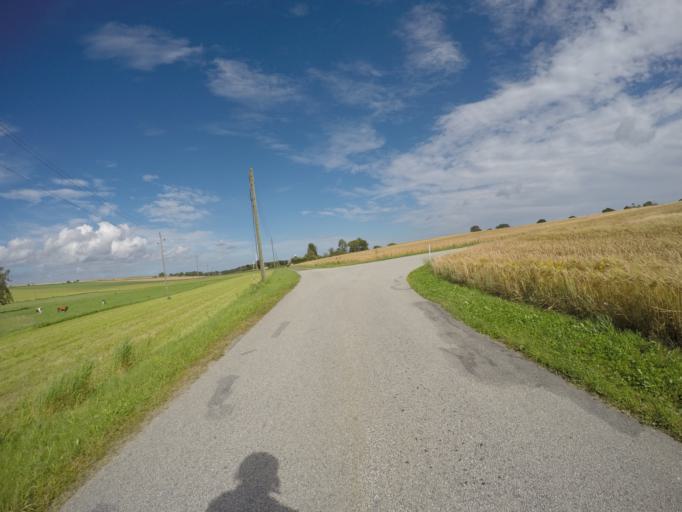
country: SE
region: Skane
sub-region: Simrishamns Kommun
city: Simrishamn
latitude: 55.4909
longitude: 14.2602
